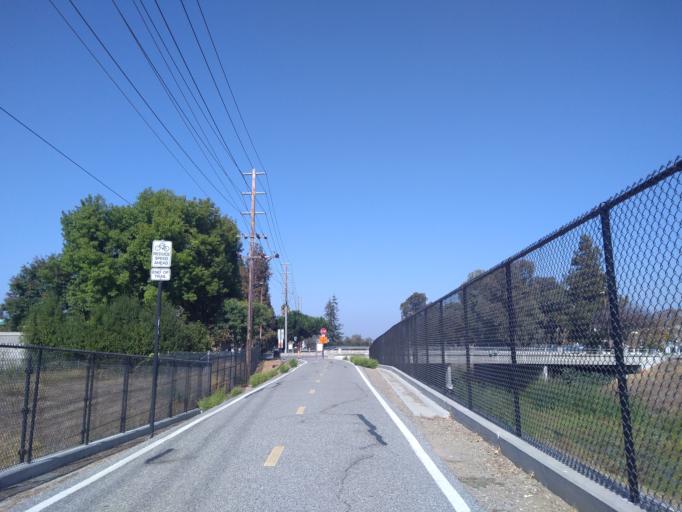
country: US
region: California
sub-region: Santa Clara County
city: Santa Clara
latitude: 37.3883
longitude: -121.9689
